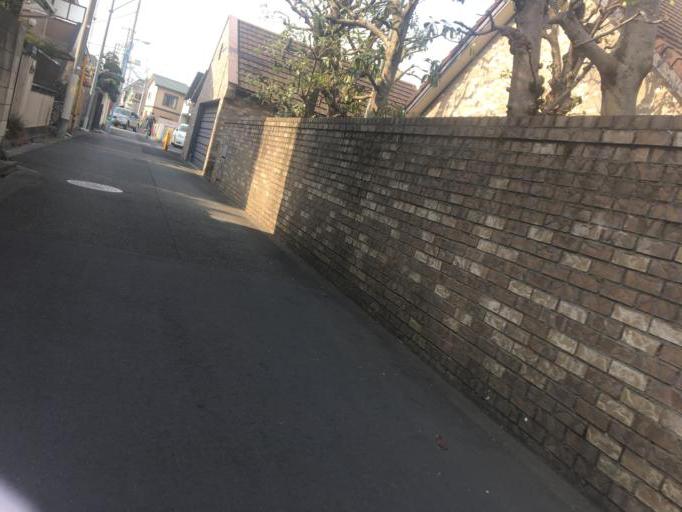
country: JP
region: Tokyo
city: Mitaka-shi
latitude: 35.6926
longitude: 139.6223
